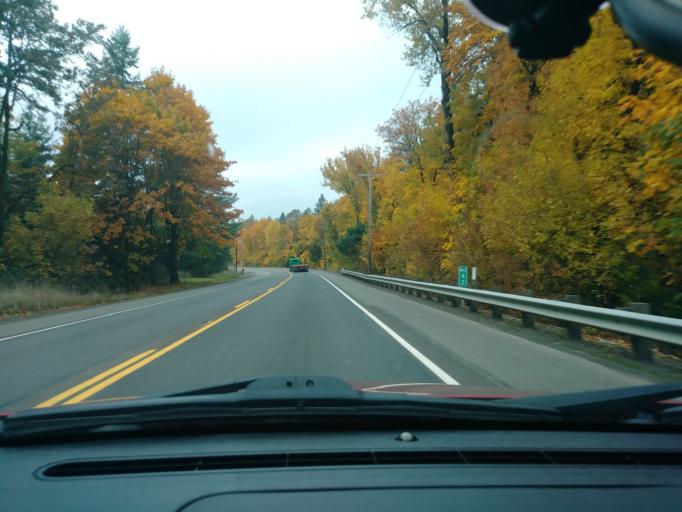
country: US
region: Oregon
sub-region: Washington County
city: Banks
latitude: 45.6150
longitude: -123.2466
